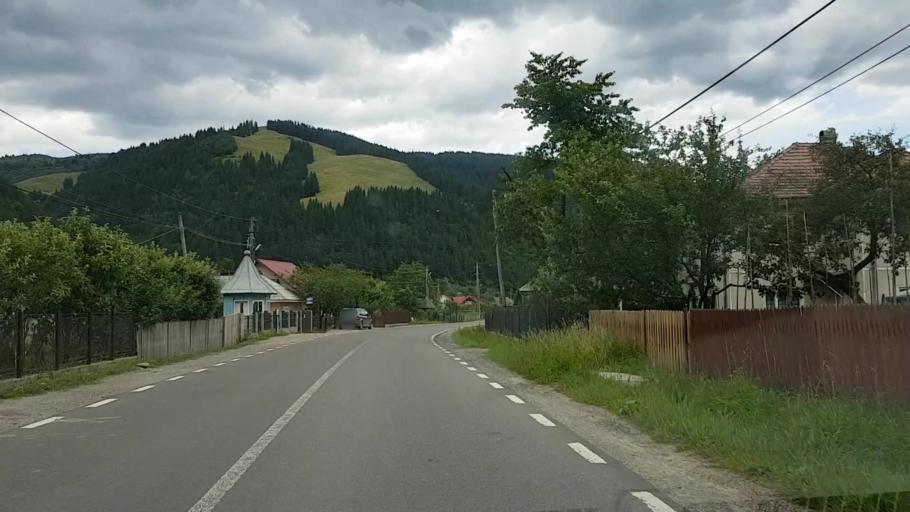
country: RO
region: Neamt
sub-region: Comuna Poiana Teiului
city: Poiana Teiului
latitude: 47.1120
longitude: 25.9293
